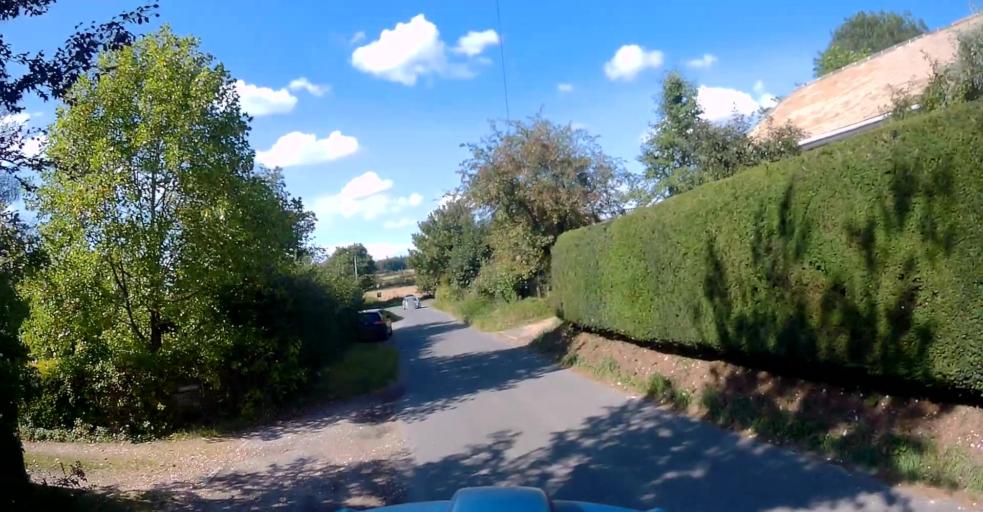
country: GB
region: England
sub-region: Hampshire
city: Four Marks
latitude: 51.1715
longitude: -1.0940
